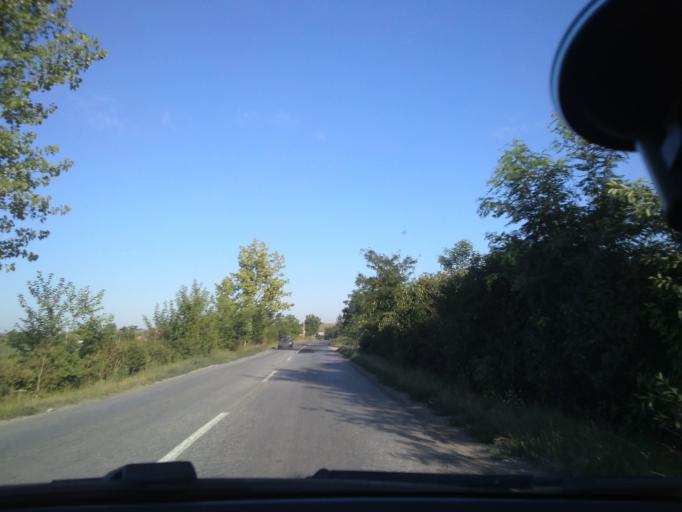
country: RS
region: Autonomna Pokrajina Vojvodina
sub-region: Zapadnobacki Okrug
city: Odzaci
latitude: 45.4593
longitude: 19.3220
